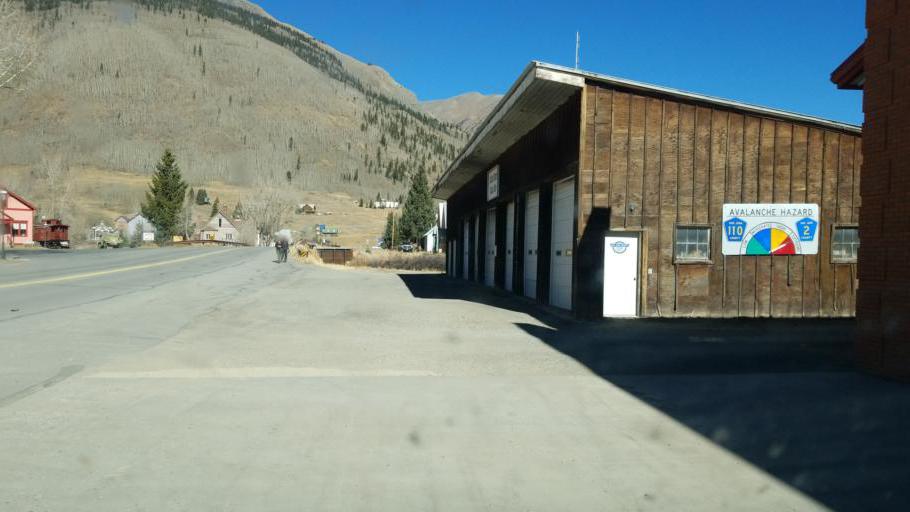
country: US
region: Colorado
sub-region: San Juan County
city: Silverton
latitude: 37.8141
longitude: -107.6619
